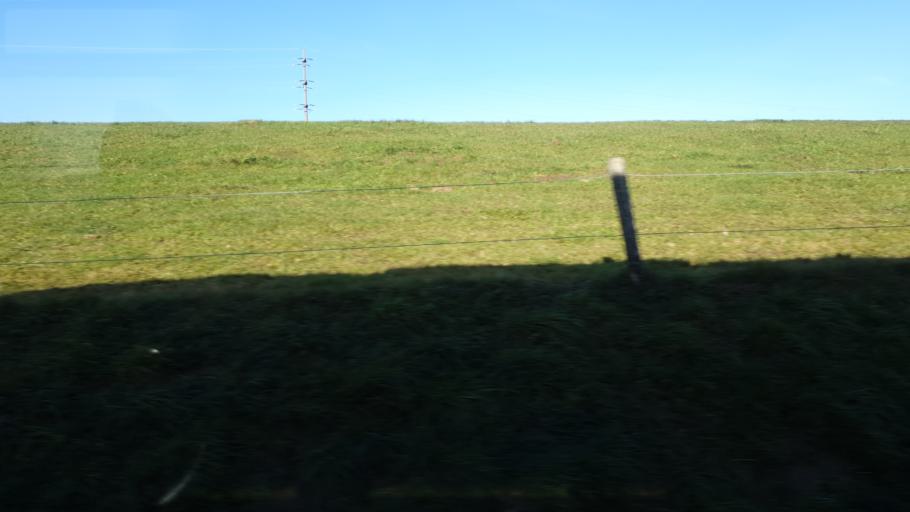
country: CH
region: Fribourg
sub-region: Gruyere District
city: Vuadens
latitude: 46.6174
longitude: 6.9960
